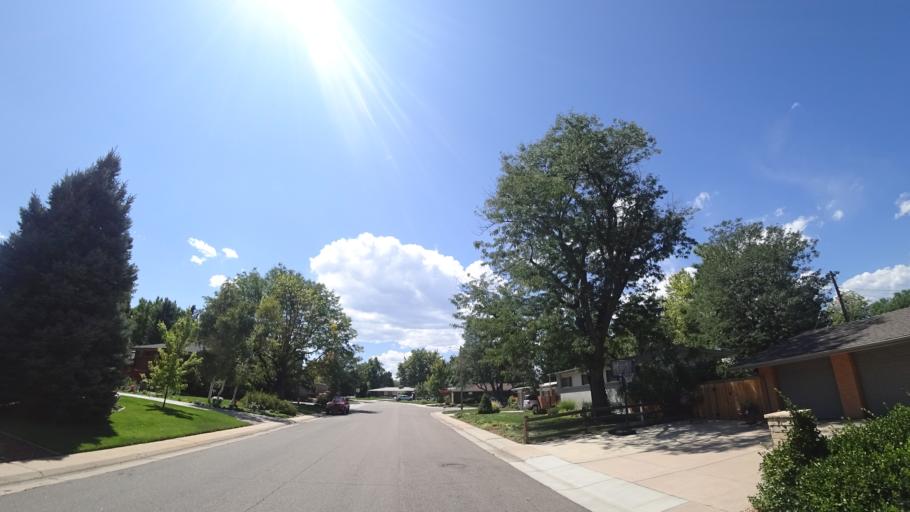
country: US
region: Colorado
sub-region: Arapahoe County
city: Littleton
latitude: 39.6061
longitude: -104.9904
